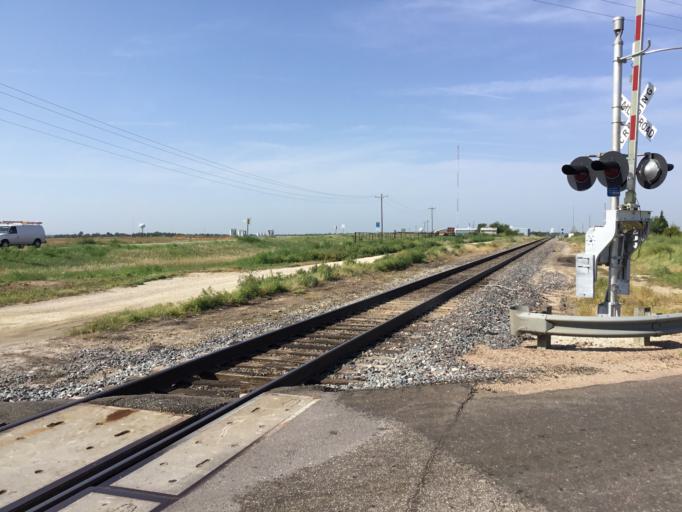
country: US
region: Kansas
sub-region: Pratt County
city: Pratt
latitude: 37.6751
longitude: -98.7113
